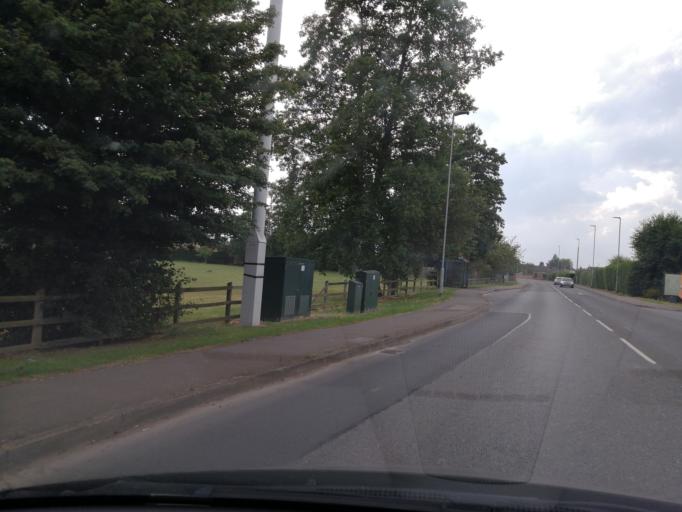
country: GB
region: England
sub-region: Peterborough
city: Peterborough
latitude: 52.5499
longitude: -0.2111
